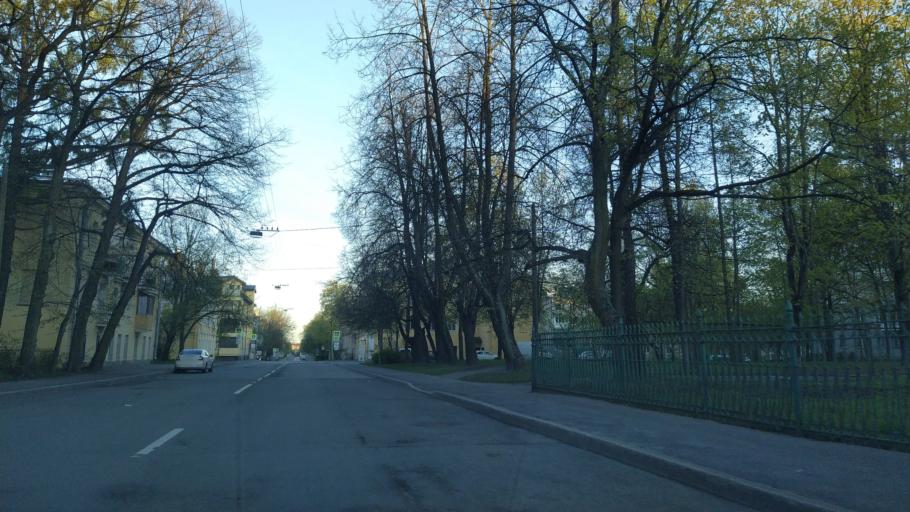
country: RU
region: St.-Petersburg
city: Pushkin
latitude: 59.7099
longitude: 30.4075
